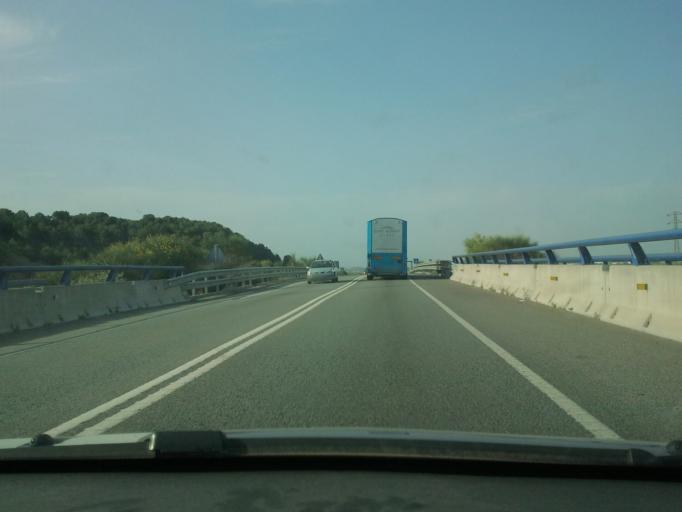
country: ES
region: Catalonia
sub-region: Provincia de Barcelona
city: Castellet
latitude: 41.2991
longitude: 1.6330
